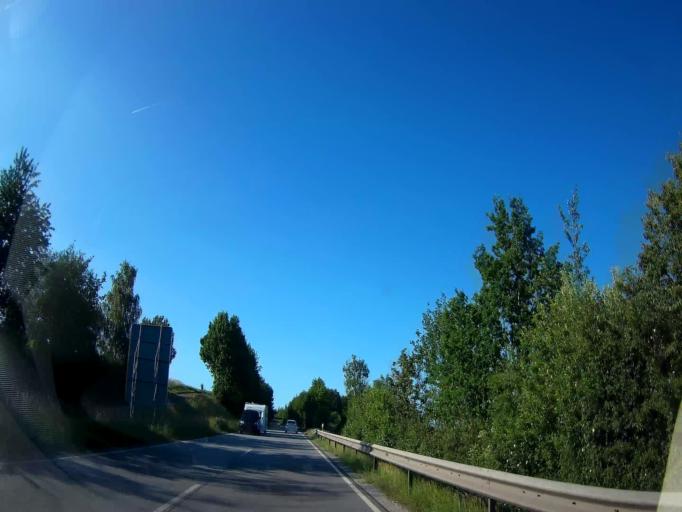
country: DE
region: Bavaria
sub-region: Lower Bavaria
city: Oberschneiding
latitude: 48.7548
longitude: 12.6616
